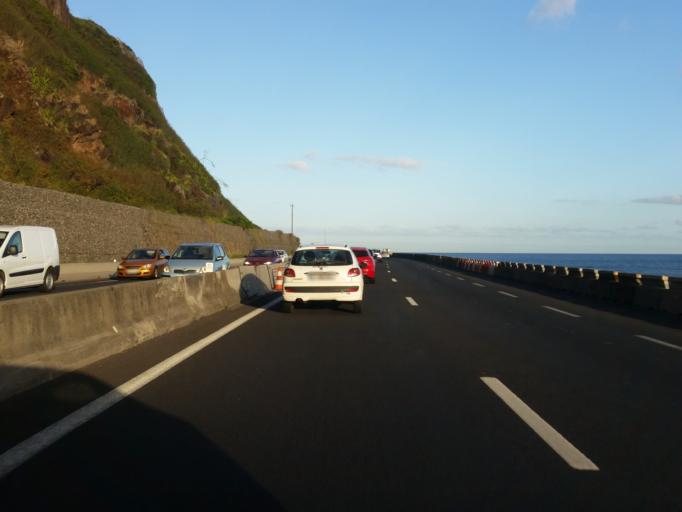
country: RE
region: Reunion
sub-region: Reunion
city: Saint-Denis
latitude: -20.8798
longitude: 55.4036
